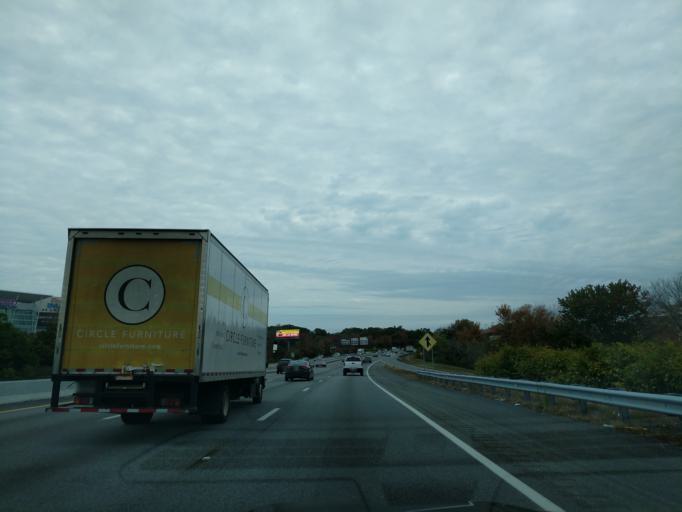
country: US
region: Massachusetts
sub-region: Middlesex County
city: Reading
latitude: 42.5175
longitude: -71.0889
